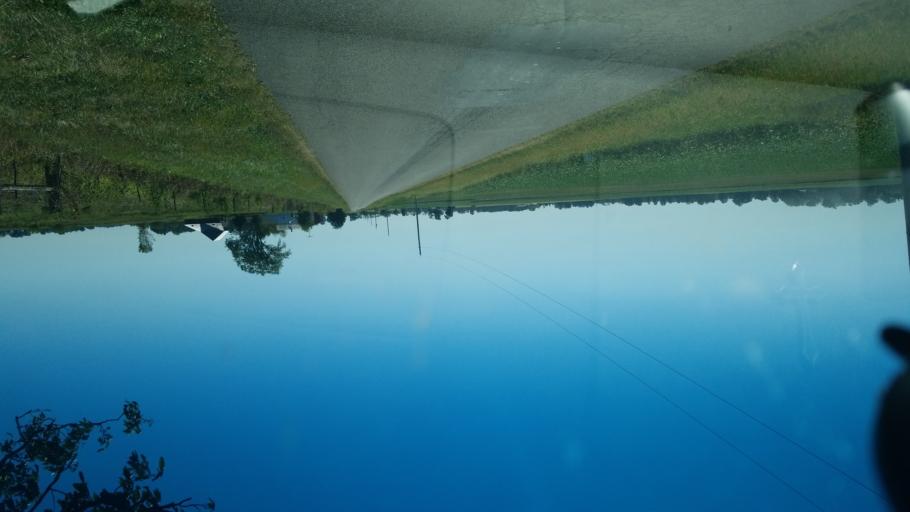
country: US
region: Ohio
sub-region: Union County
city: Richwood
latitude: 40.4703
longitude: -83.2559
